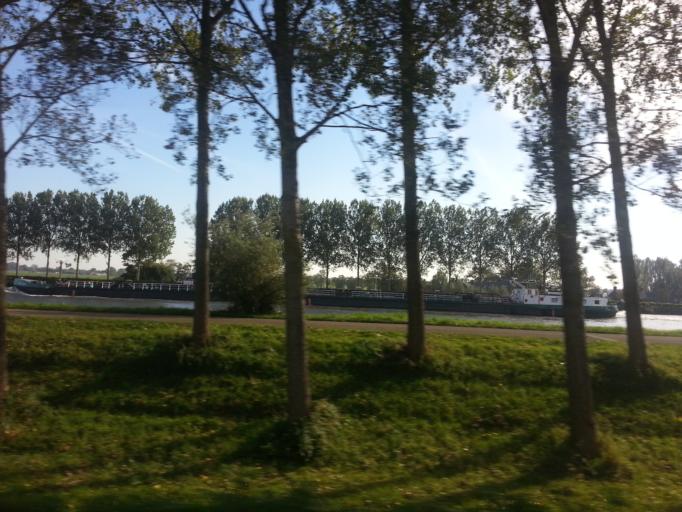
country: NL
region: Utrecht
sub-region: Stichtse Vecht
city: Vreeland
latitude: 52.2312
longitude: 5.0068
